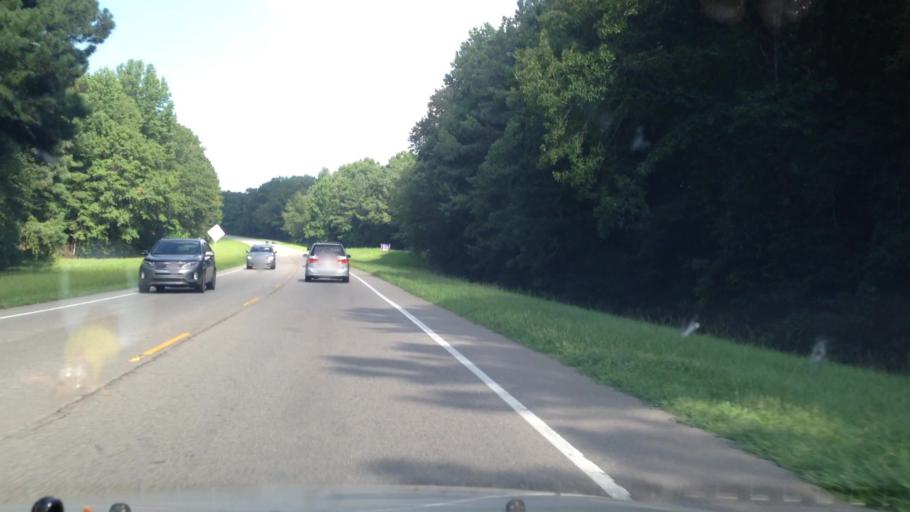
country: US
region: North Carolina
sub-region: Lee County
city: Broadway
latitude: 35.4380
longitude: -79.0643
